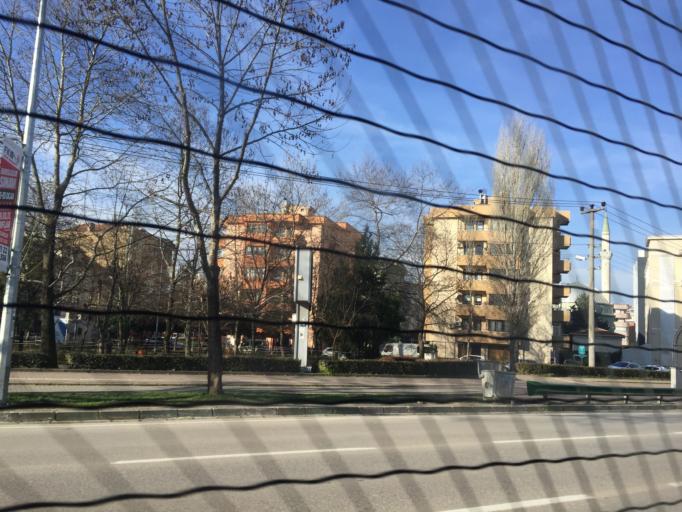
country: TR
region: Bursa
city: Yildirim
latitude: 40.2228
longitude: 28.9940
